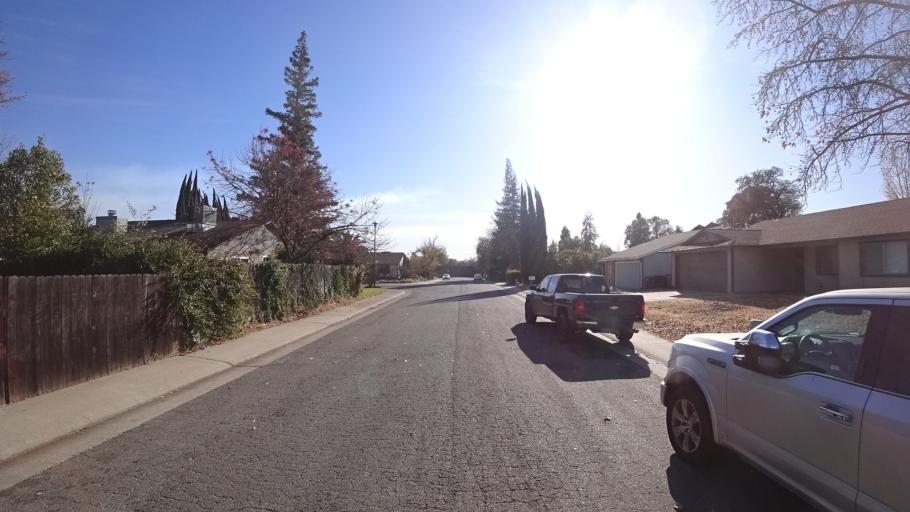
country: US
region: California
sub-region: Sacramento County
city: Antelope
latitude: 38.6946
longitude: -121.3261
